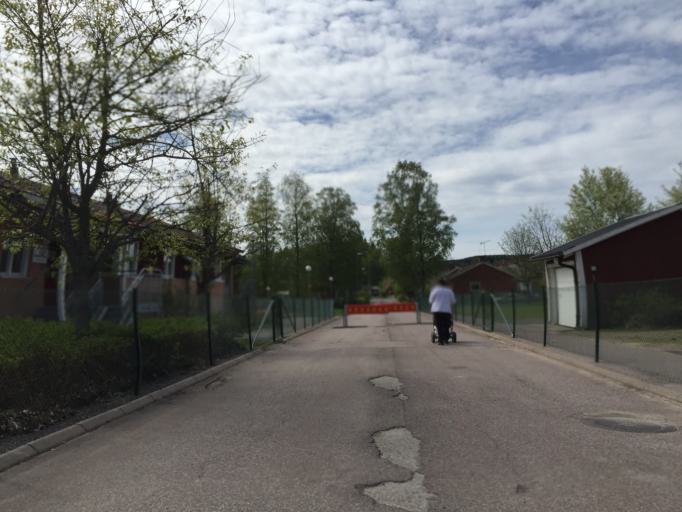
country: SE
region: Dalarna
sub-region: Ludvika Kommun
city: Ludvika
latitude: 60.1269
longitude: 15.1886
